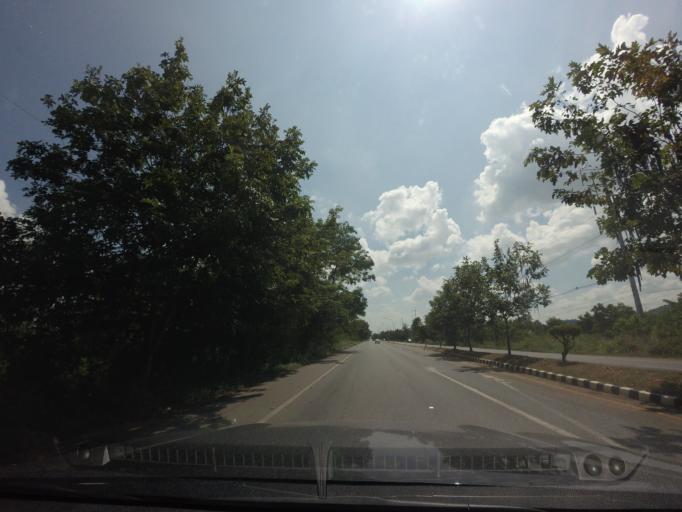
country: TH
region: Phetchabun
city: Nong Phai
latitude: 16.0411
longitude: 101.0795
